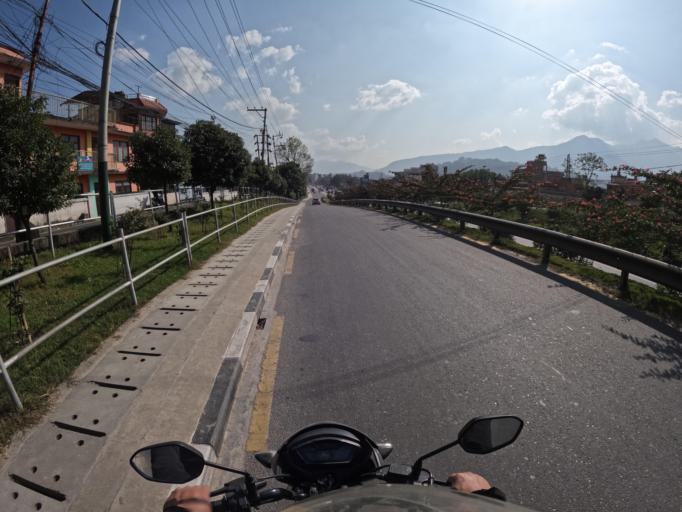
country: NP
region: Central Region
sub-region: Bagmati Zone
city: Patan
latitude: 27.6794
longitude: 85.3024
